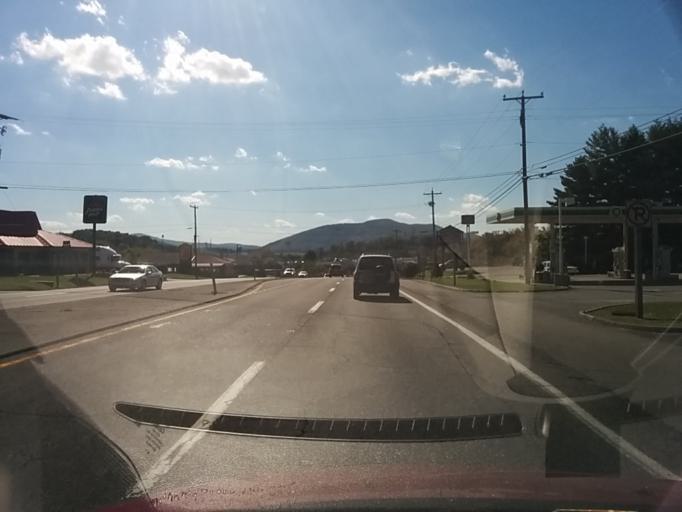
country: US
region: Virginia
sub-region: Botetourt County
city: Daleville
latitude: 37.3935
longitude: -79.9064
